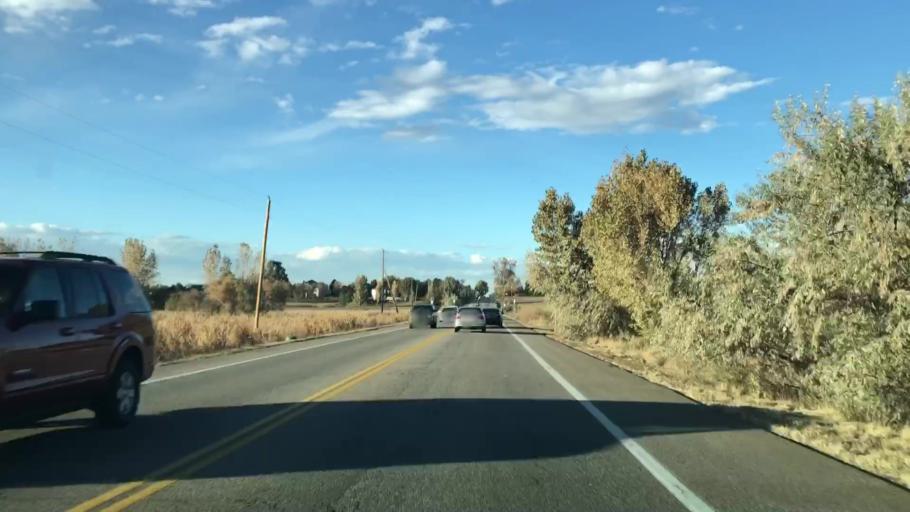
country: US
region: Colorado
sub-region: Larimer County
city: Loveland
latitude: 40.4863
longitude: -105.0393
